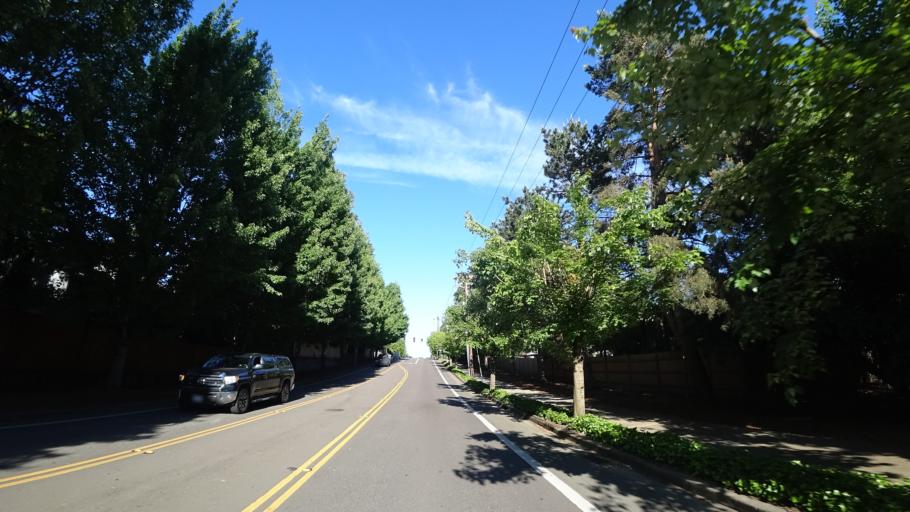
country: US
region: Oregon
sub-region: Washington County
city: Beaverton
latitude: 45.4548
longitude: -122.8096
